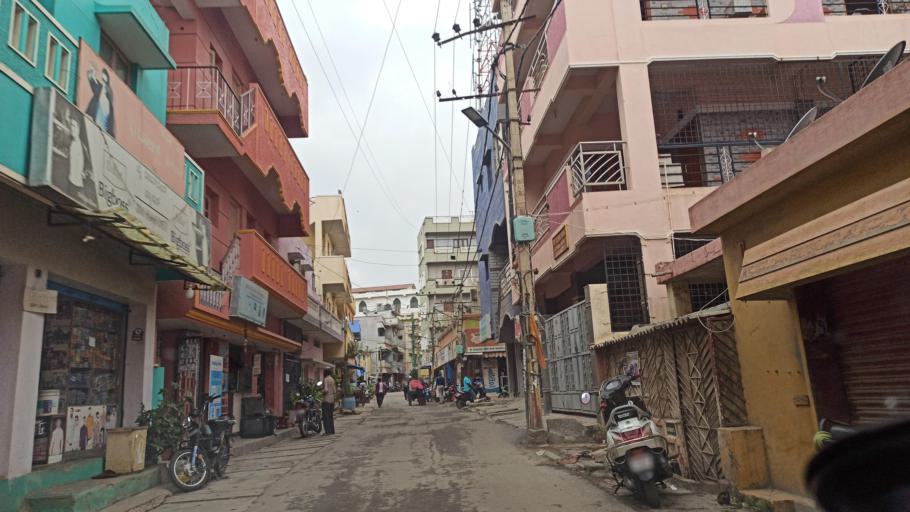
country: IN
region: Karnataka
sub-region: Bangalore Urban
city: Bangalore
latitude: 12.9944
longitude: 77.6751
